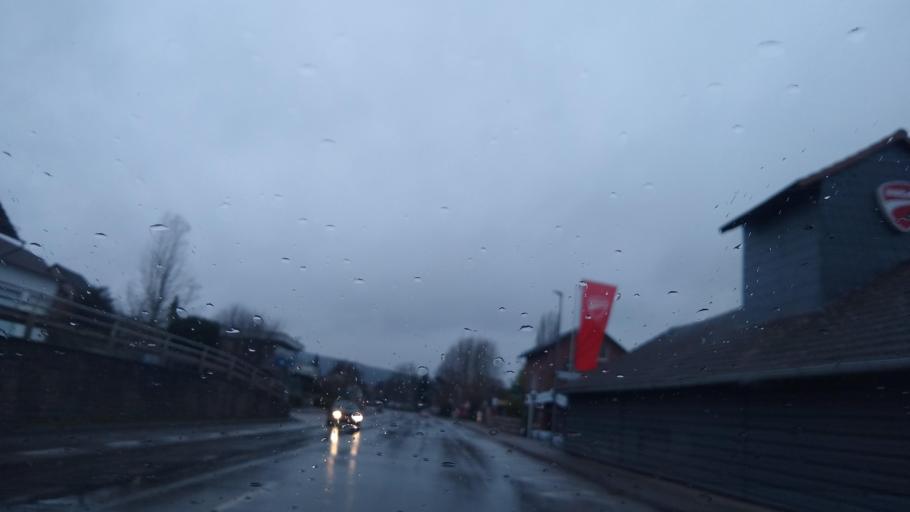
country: DE
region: Lower Saxony
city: Hehlen
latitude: 51.9855
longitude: 9.4751
